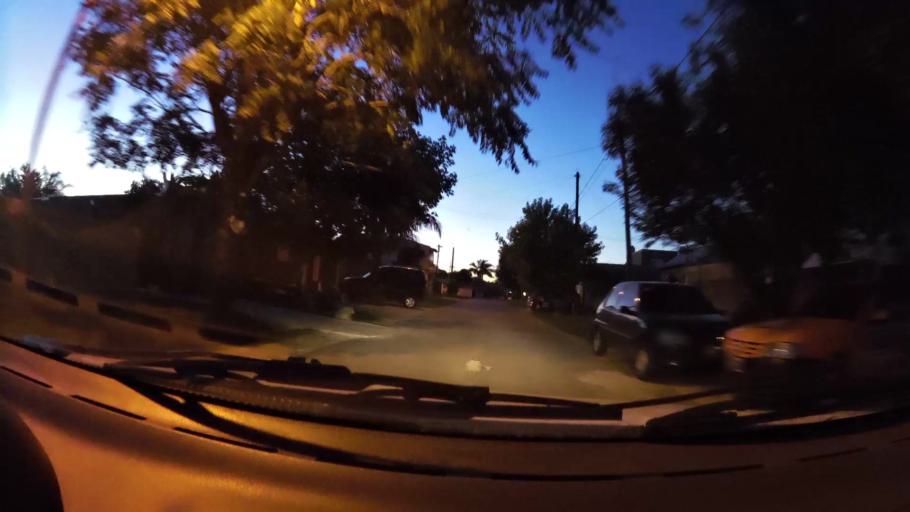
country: AR
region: Buenos Aires
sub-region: Partido de Quilmes
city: Quilmes
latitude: -34.7779
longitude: -58.1838
